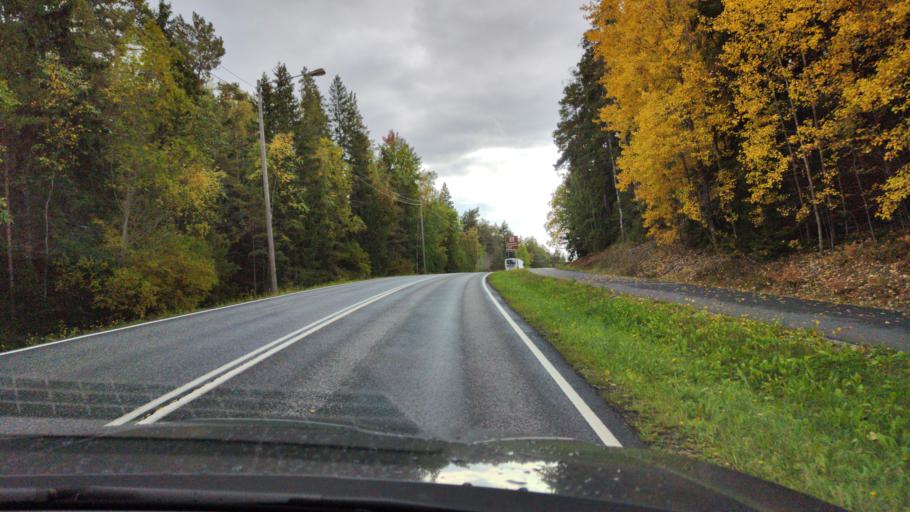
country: FI
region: Varsinais-Suomi
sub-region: Turku
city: Raisio
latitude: 60.3623
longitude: 22.1784
